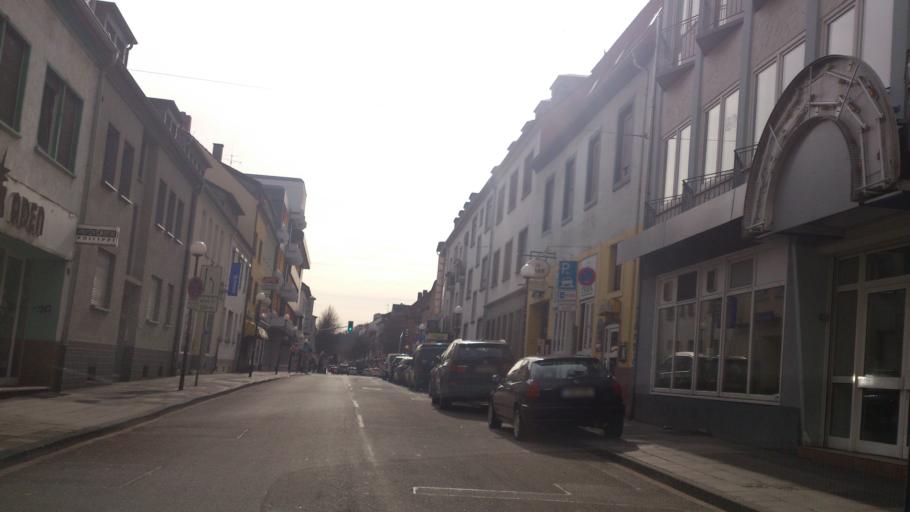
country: DE
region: Rheinland-Pfalz
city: Zweibrucken
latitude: 49.2483
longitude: 7.3668
